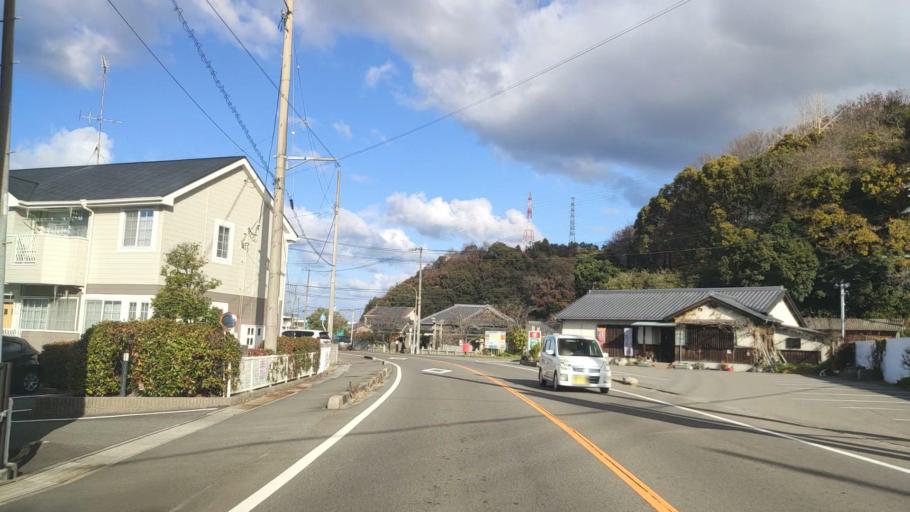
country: JP
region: Ehime
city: Masaki-cho
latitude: 33.8403
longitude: 132.7092
